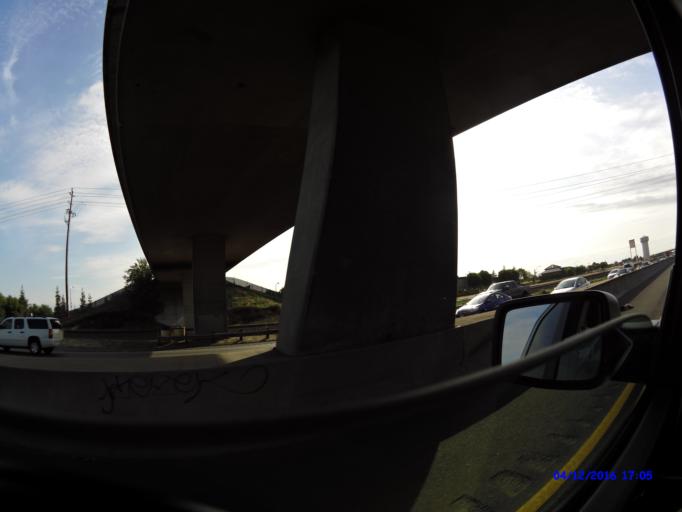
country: US
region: California
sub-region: San Joaquin County
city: Ripon
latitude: 37.7465
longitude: -121.1331
